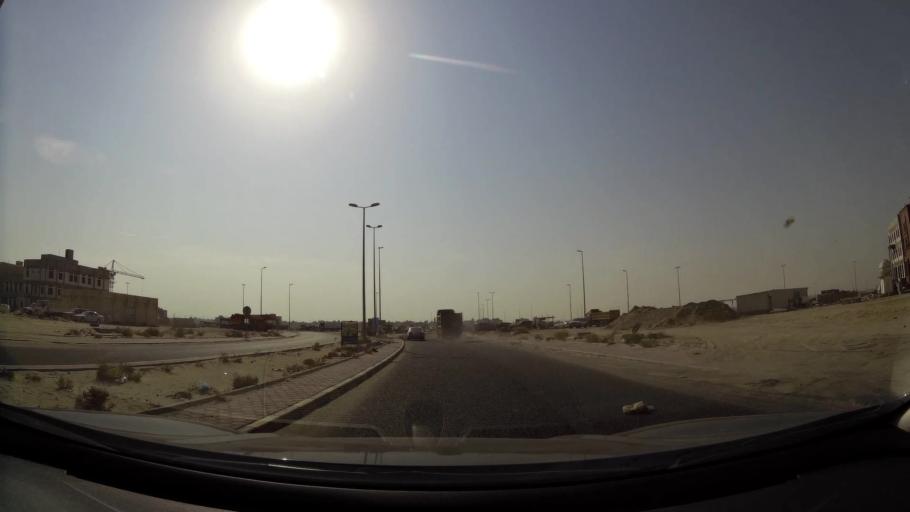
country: KW
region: Al Ahmadi
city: Al Wafrah
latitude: 28.7832
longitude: 48.0510
